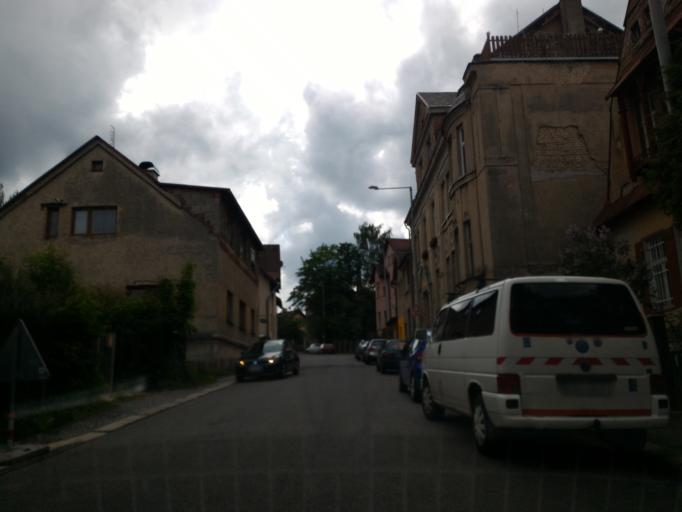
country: CZ
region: Liberecky
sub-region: Okres Jablonec nad Nisou
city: Jablonec nad Nisou
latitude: 50.7223
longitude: 15.1776
